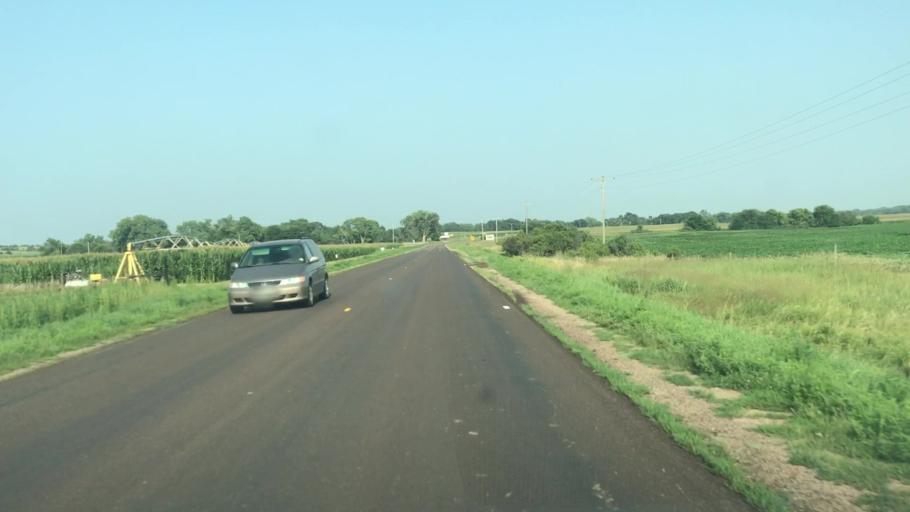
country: US
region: Nebraska
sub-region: Buffalo County
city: Ravenna
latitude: 41.0756
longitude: -98.7350
